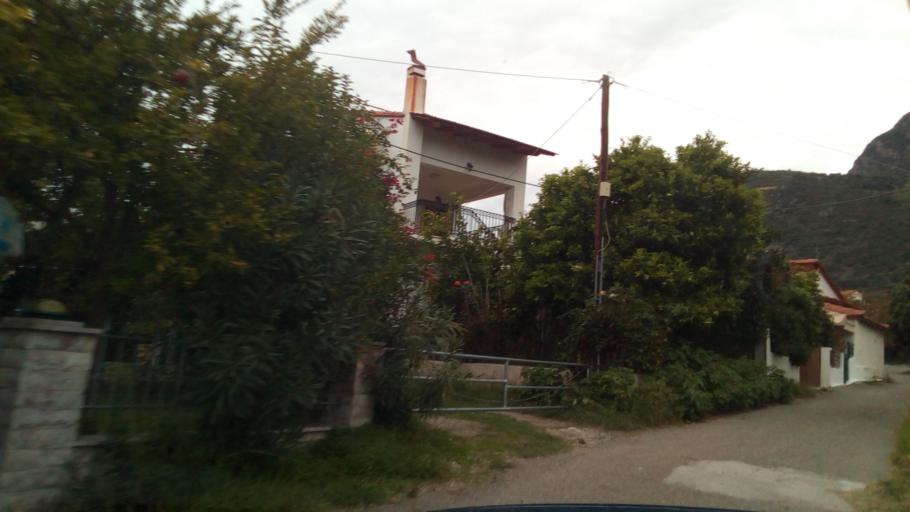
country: GR
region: West Greece
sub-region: Nomos Achaias
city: Kamarai
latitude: 38.3938
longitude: 22.0160
